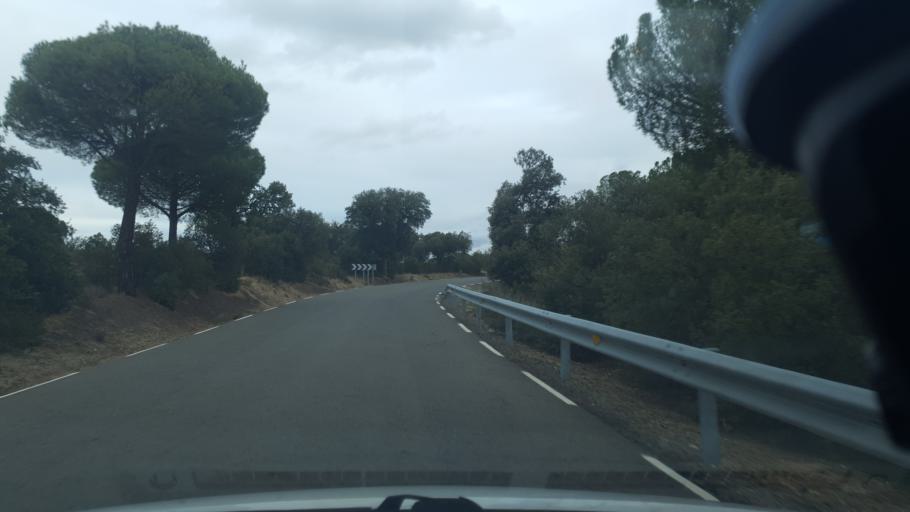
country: ES
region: Castille and Leon
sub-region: Provincia de Avila
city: Pozanco
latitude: 40.8245
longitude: -4.6833
